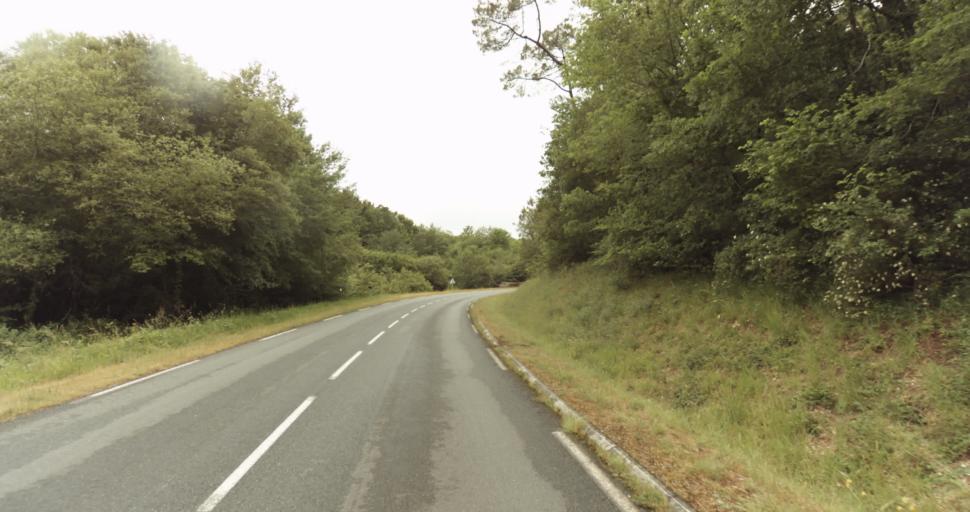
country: FR
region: Aquitaine
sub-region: Departement de la Dordogne
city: Belves
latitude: 44.6660
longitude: 1.0078
